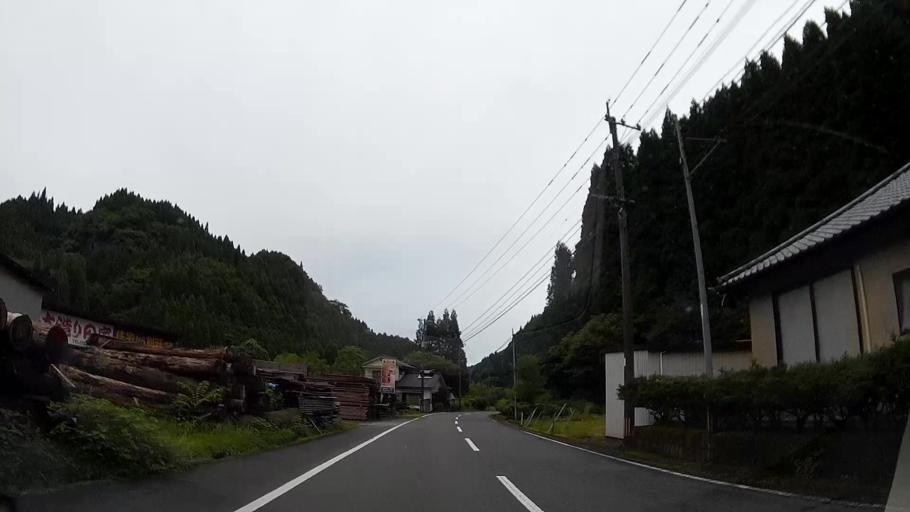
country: JP
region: Kumamoto
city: Kikuchi
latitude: 33.1079
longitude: 130.9606
